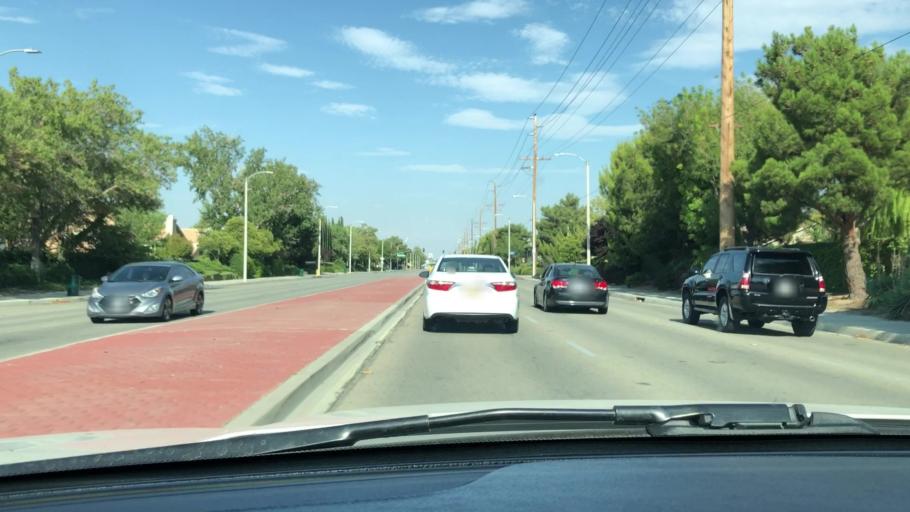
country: US
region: California
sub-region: Los Angeles County
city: Lancaster
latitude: 34.6894
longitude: -118.1823
